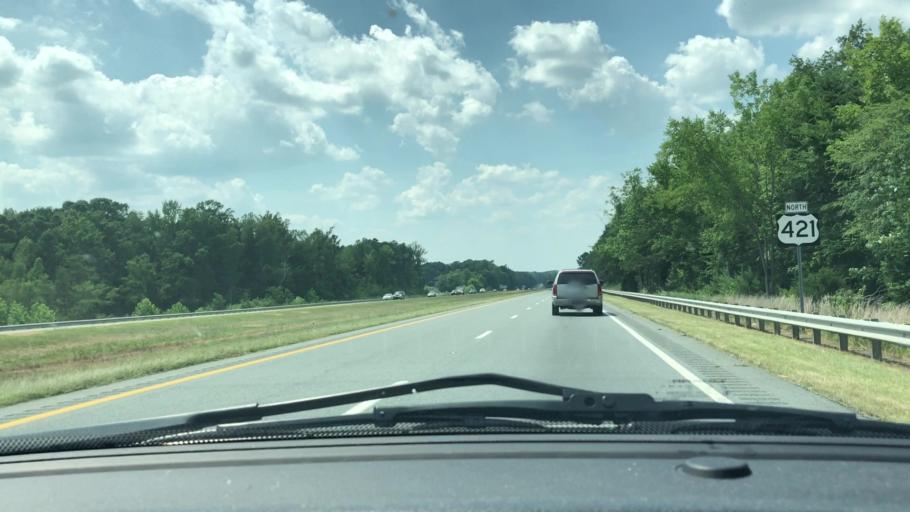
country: US
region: North Carolina
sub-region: Guilford County
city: Forest Oaks
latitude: 35.9682
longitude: -79.7131
